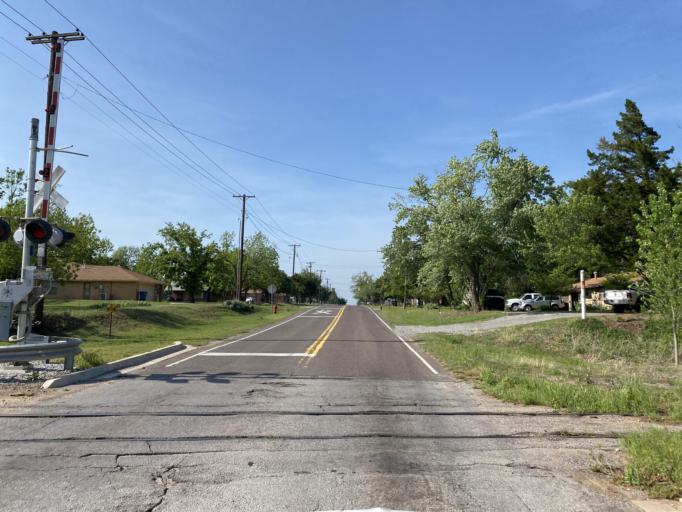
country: US
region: Oklahoma
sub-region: Oklahoma County
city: Nicoma Park
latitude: 35.4844
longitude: -97.3356
